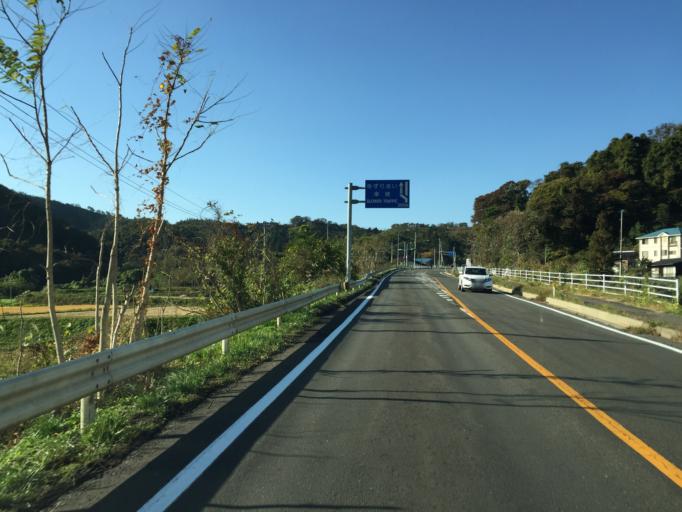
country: JP
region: Fukushima
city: Yanagawamachi-saiwaicho
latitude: 37.9144
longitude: 140.5918
